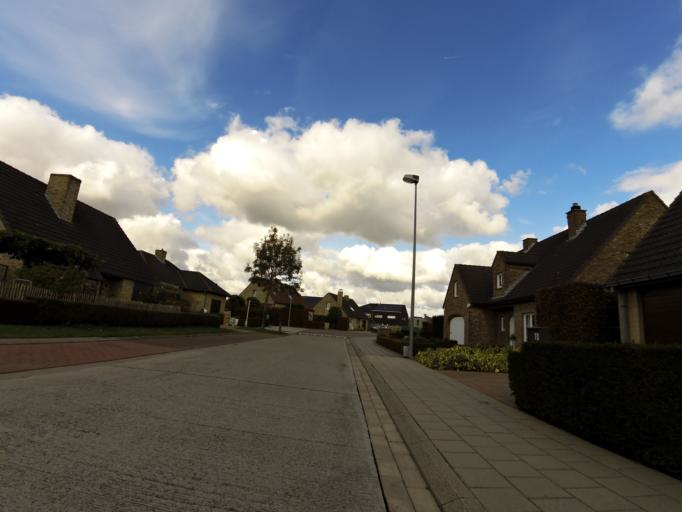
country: BE
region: Flanders
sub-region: Provincie West-Vlaanderen
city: Sint-Kruis
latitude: 51.2313
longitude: 3.2364
